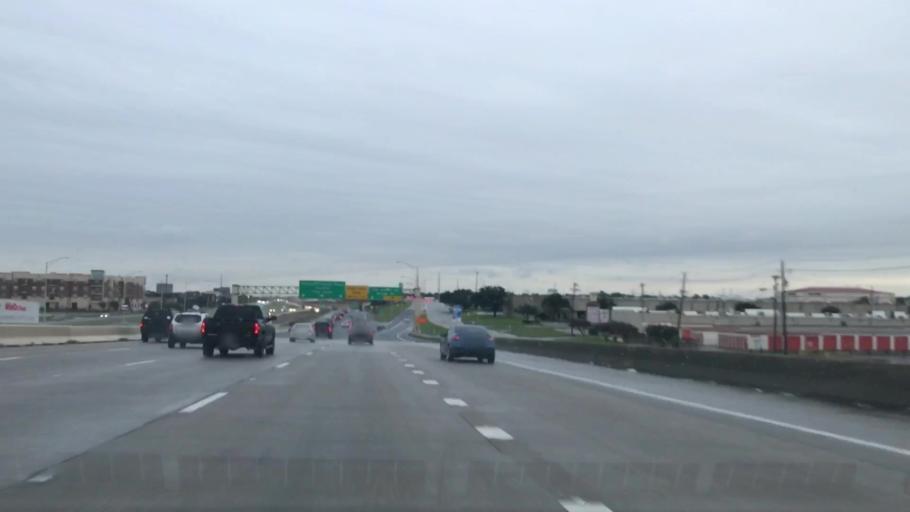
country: US
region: Texas
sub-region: Dallas County
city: Carrollton
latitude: 32.9831
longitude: -96.9182
